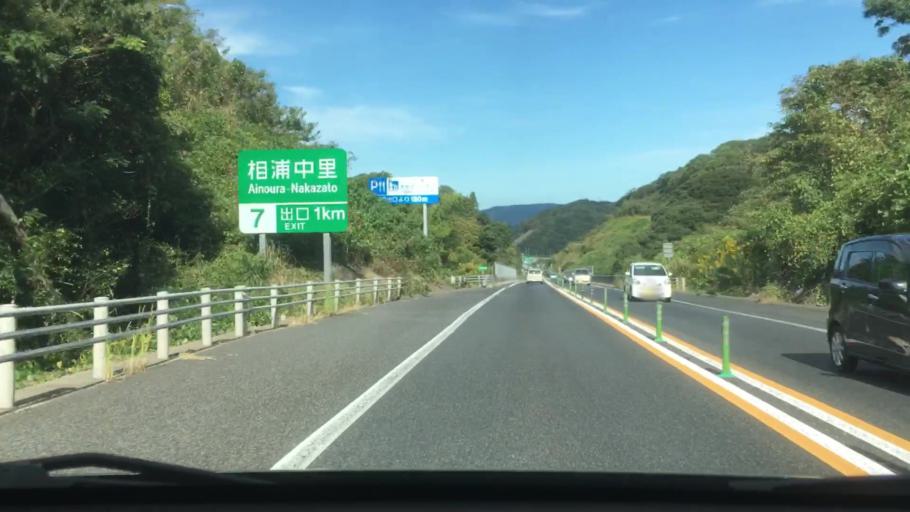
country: JP
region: Nagasaki
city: Sasebo
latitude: 33.1947
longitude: 129.6796
